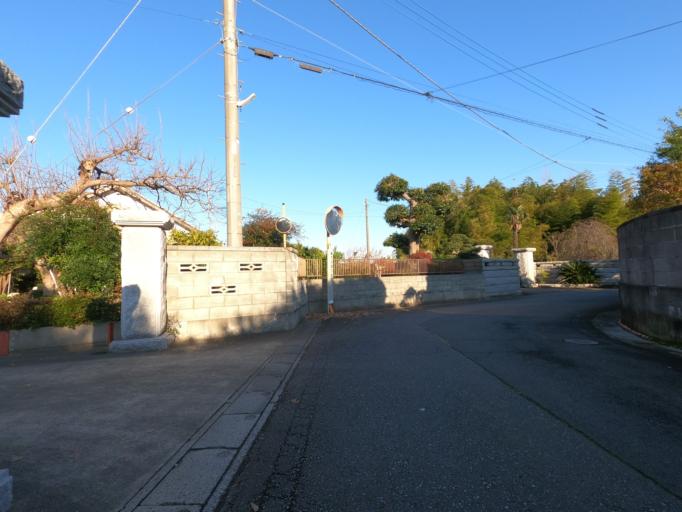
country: JP
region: Ibaraki
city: Moriya
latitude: 35.9316
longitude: 139.9998
